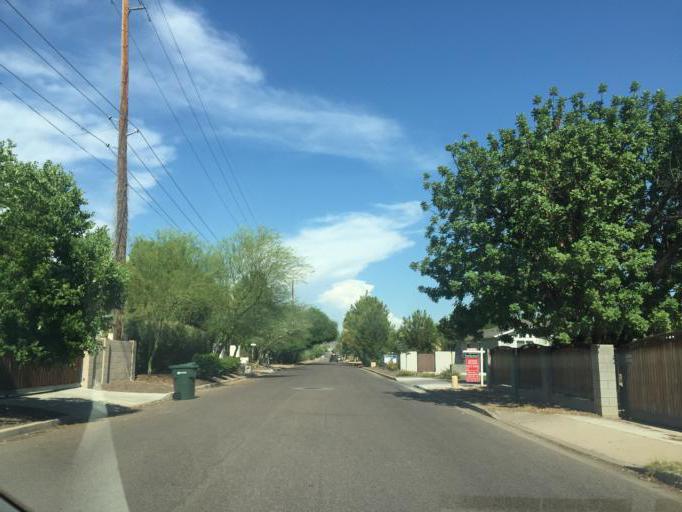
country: US
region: Arizona
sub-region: Maricopa County
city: Phoenix
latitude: 33.5346
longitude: -112.0534
